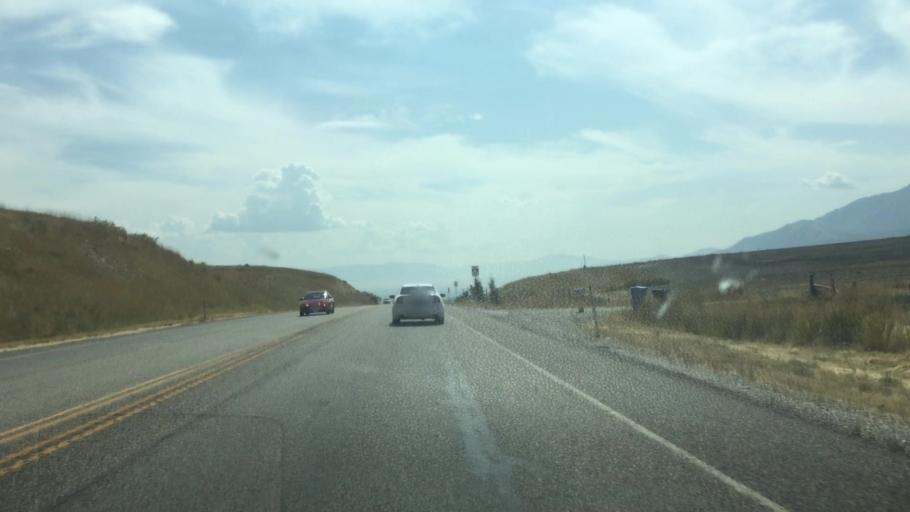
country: US
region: Utah
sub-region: Cache County
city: Mendon
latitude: 41.7709
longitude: -112.0159
